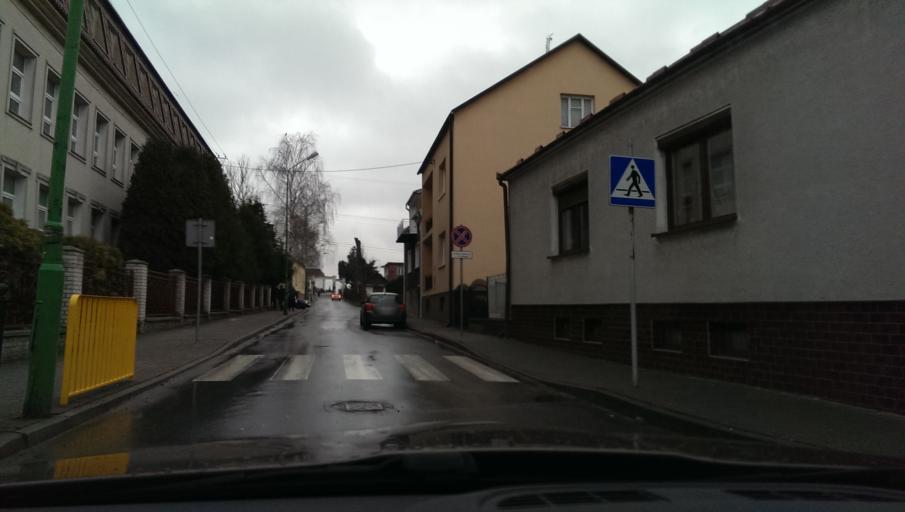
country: PL
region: Subcarpathian Voivodeship
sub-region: Powiat ropczycko-sedziszowski
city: Sedziszow Malopolski
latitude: 50.0703
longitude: 21.7030
